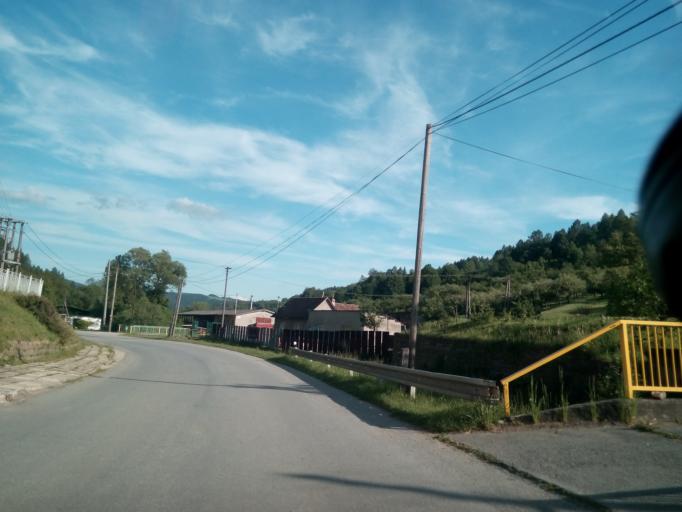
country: SK
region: Presovsky
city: Lipany
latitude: 49.0362
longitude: 20.9445
